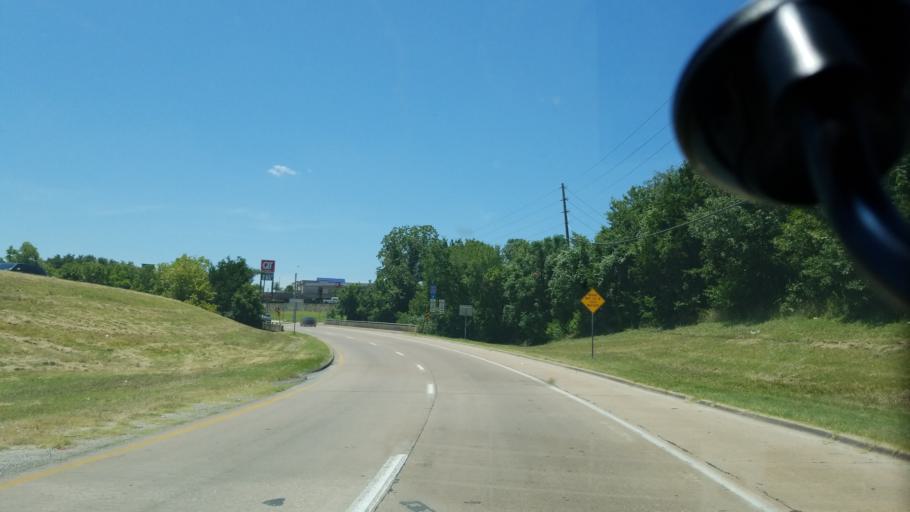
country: US
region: Texas
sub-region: Dallas County
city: Cockrell Hill
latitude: 32.6889
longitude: -96.8243
